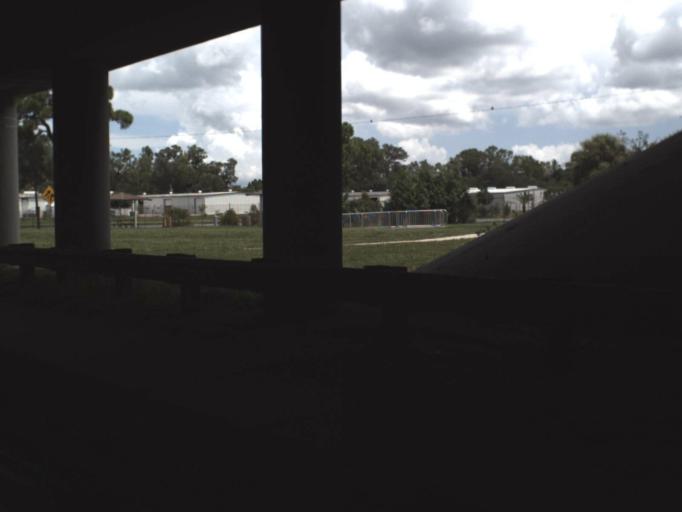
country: US
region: Florida
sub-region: Pinellas County
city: Pinellas Park
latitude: 27.8623
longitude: -82.7001
